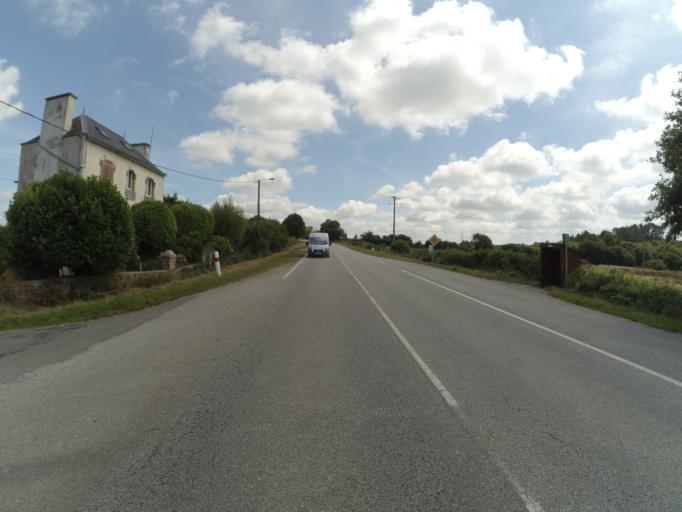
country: FR
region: Brittany
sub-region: Departement du Finistere
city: Saint-Yvi
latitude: 47.9704
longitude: -3.9737
